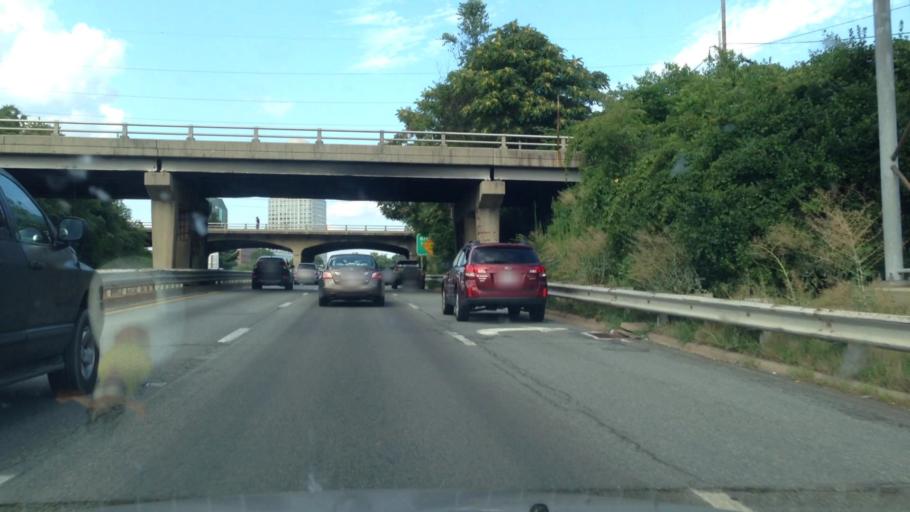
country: US
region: North Carolina
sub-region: Forsyth County
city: Winston-Salem
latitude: 36.0913
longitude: -80.2529
